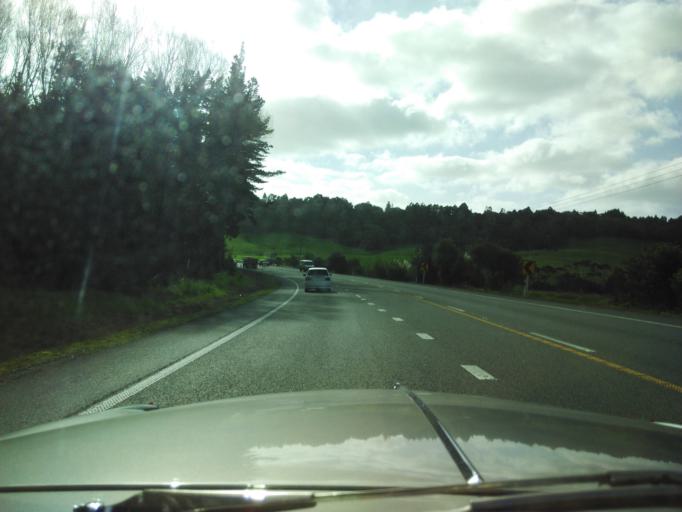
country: NZ
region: Auckland
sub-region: Auckland
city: Warkworth
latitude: -36.4334
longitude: 174.6496
